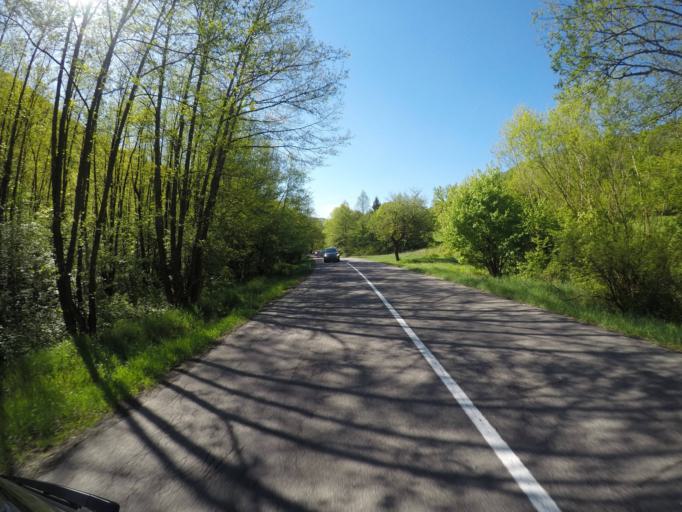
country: SK
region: Banskobystricky
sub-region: Okres Banska Bystrica
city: Banska Stiavnica
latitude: 48.5436
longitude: 19.0037
